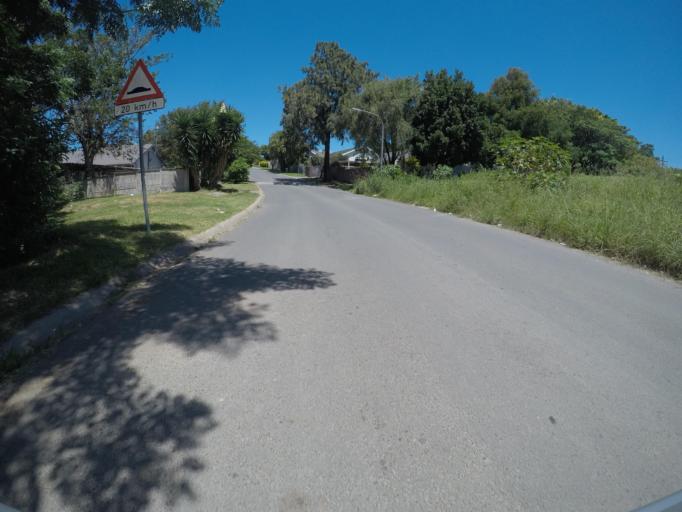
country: ZA
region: Eastern Cape
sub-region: Buffalo City Metropolitan Municipality
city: East London
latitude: -32.9558
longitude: 27.9370
